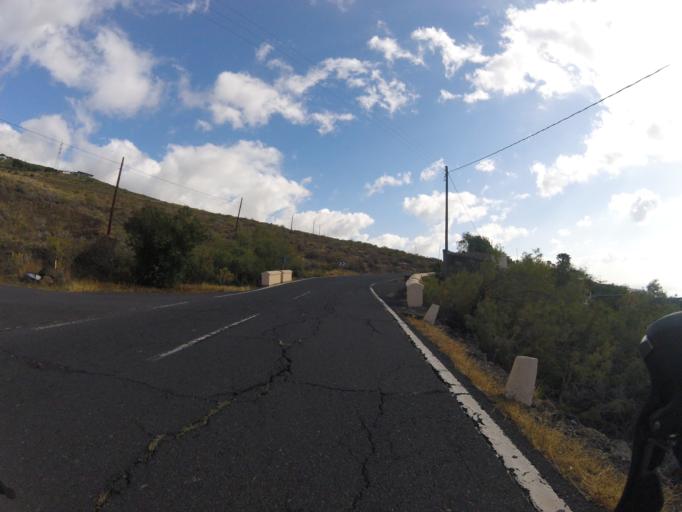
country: ES
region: Canary Islands
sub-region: Provincia de Santa Cruz de Tenerife
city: Candelaria
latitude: 28.3921
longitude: -16.3518
